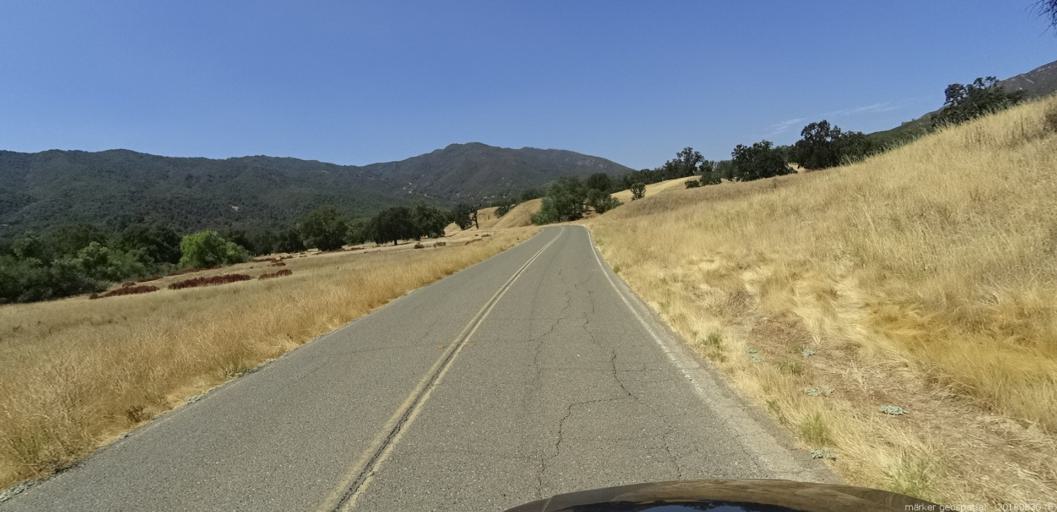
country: US
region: California
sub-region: Monterey County
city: King City
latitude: 35.9760
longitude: -121.3368
